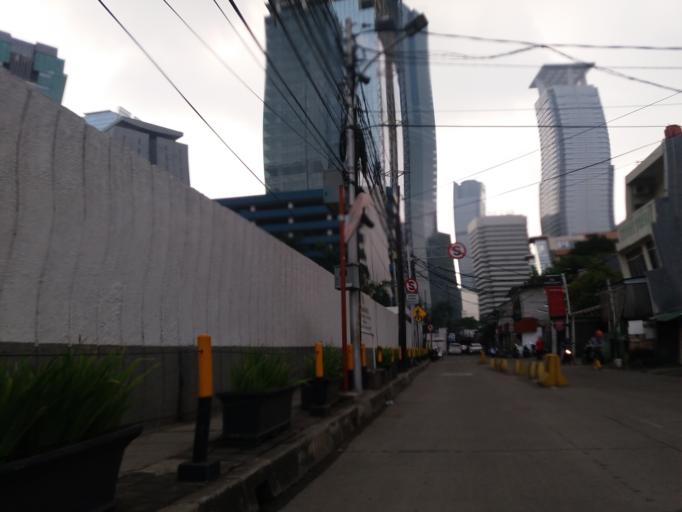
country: ID
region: Jakarta Raya
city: Jakarta
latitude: -6.2147
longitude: 106.8218
